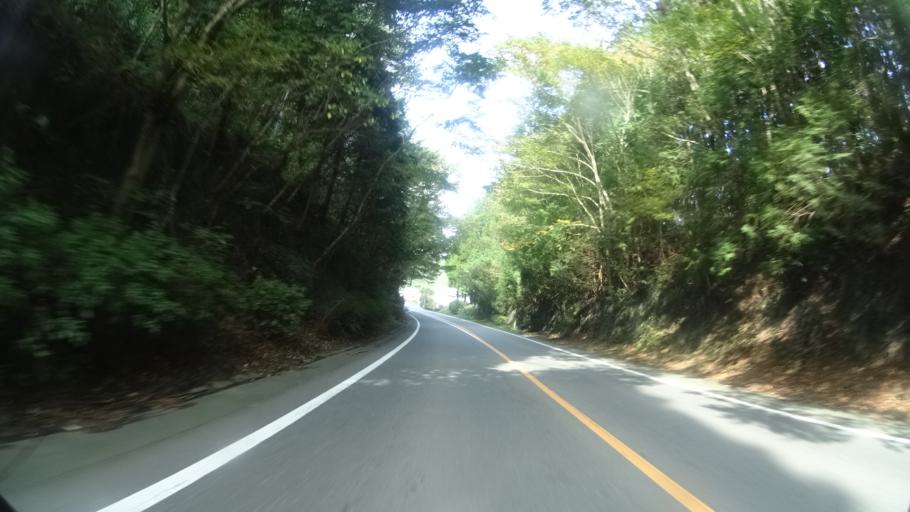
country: JP
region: Kumamoto
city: Aso
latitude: 33.0873
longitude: 131.0675
